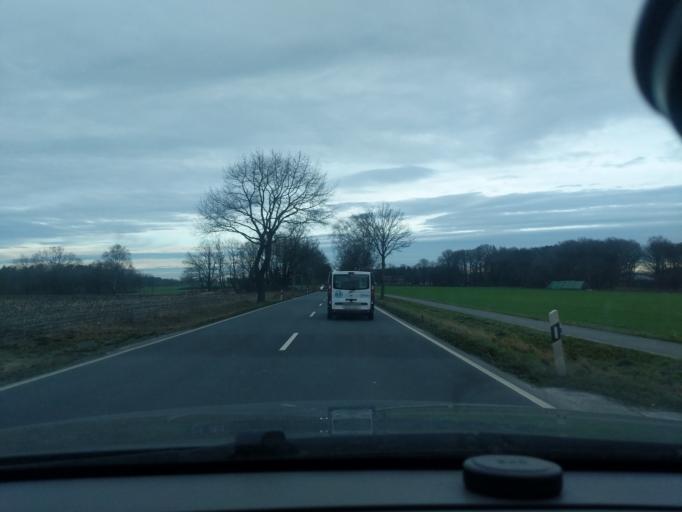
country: DE
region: Lower Saxony
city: Halvesbostel
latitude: 53.3636
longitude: 9.5855
